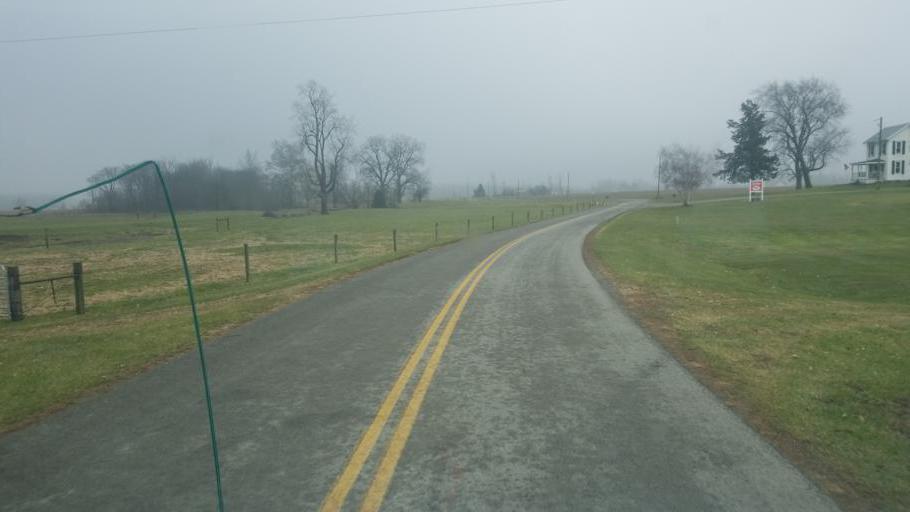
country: US
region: Ohio
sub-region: Hardin County
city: Kenton
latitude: 40.5035
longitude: -83.5298
